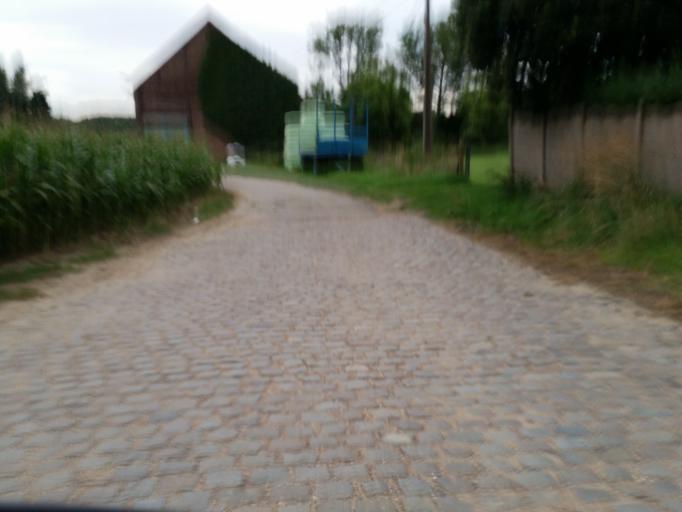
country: BE
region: Flanders
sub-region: Provincie Vlaams-Brabant
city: Zemst
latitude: 50.9875
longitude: 4.4593
